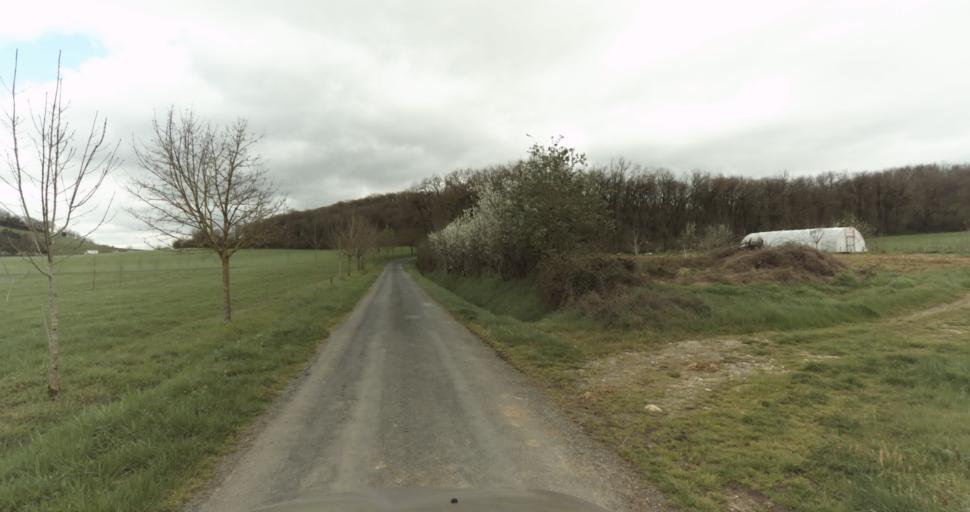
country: FR
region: Midi-Pyrenees
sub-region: Departement du Tarn
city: Puygouzon
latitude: 43.8690
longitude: 2.1804
